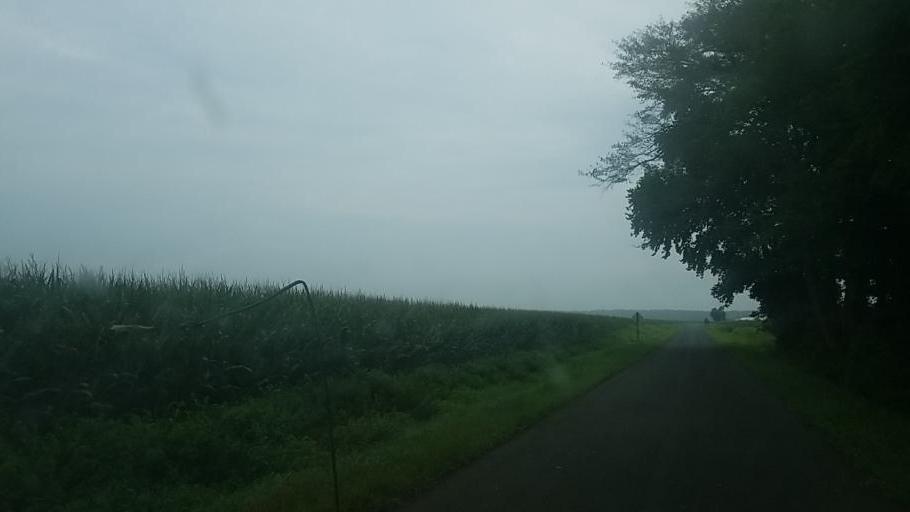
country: US
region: Delaware
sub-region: Sussex County
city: Selbyville
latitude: 38.4390
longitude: -75.2910
